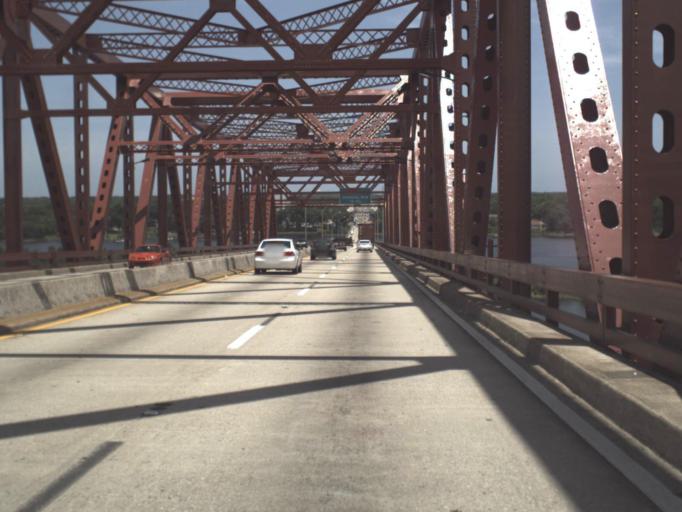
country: US
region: Florida
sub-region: Duval County
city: Jacksonville
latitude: 30.3272
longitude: -81.6204
